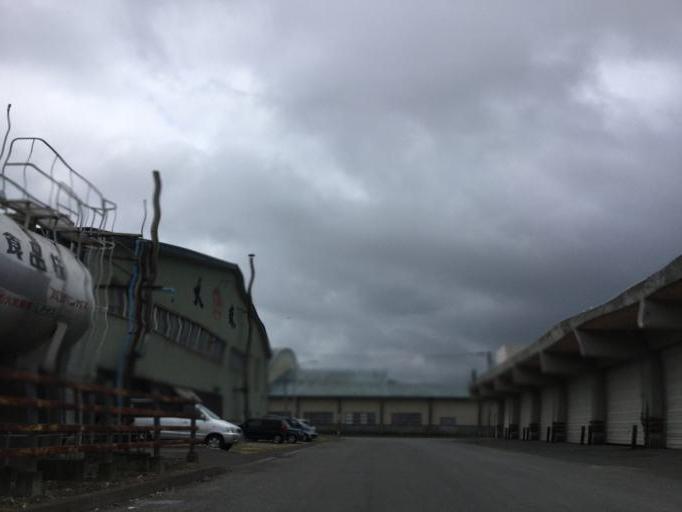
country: JP
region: Hokkaido
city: Wakkanai
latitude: 45.4073
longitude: 141.6797
